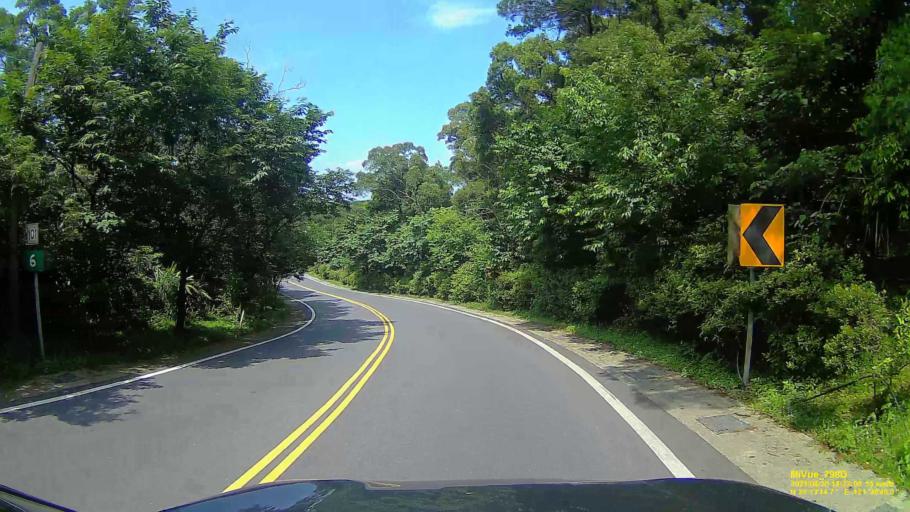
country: TW
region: Taipei
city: Taipei
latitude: 25.2208
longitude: 121.5130
